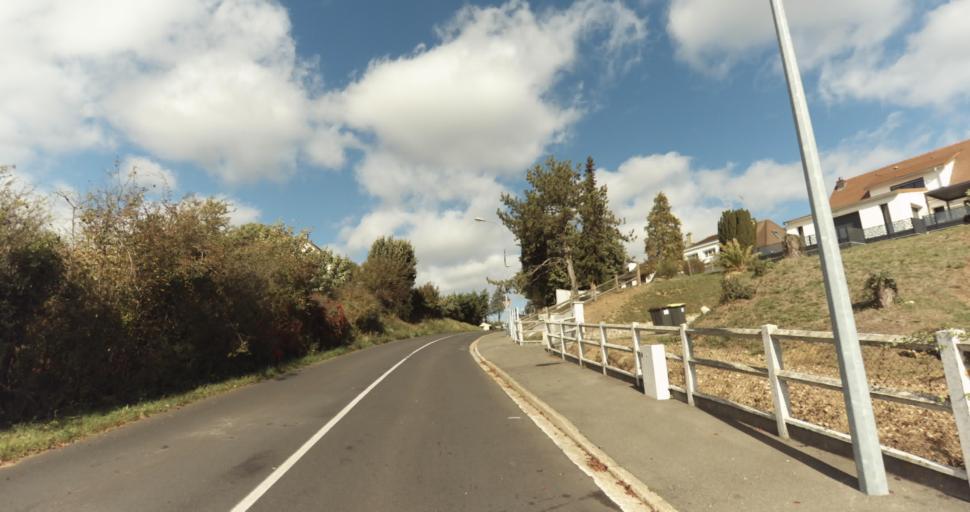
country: FR
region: Centre
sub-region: Departement d'Eure-et-Loir
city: Garnay
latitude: 48.7220
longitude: 1.3263
